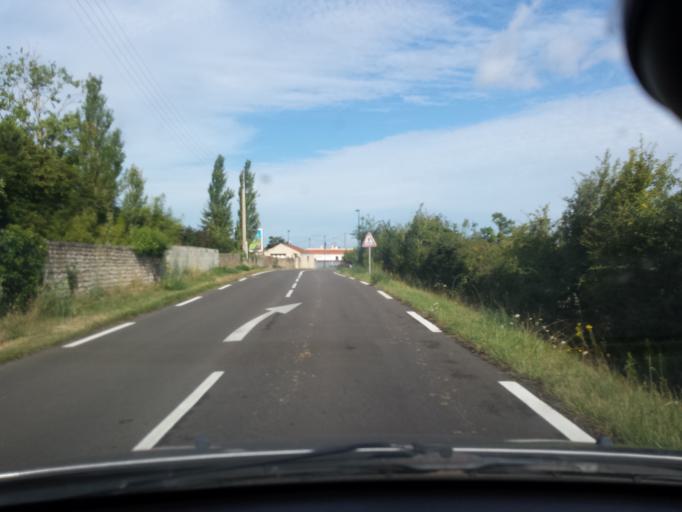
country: FR
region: Pays de la Loire
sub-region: Departement de la Vendee
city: Olonne-sur-Mer
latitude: 46.5398
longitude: -1.7938
